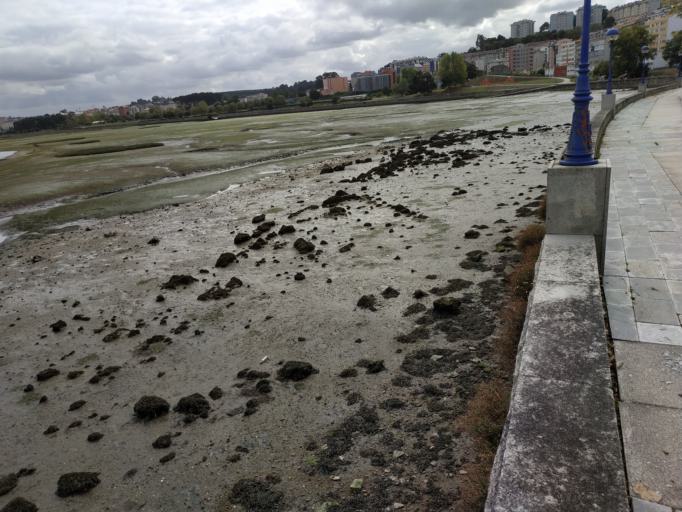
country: ES
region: Galicia
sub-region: Provincia da Coruna
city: Culleredo
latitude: 43.3274
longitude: -8.3794
